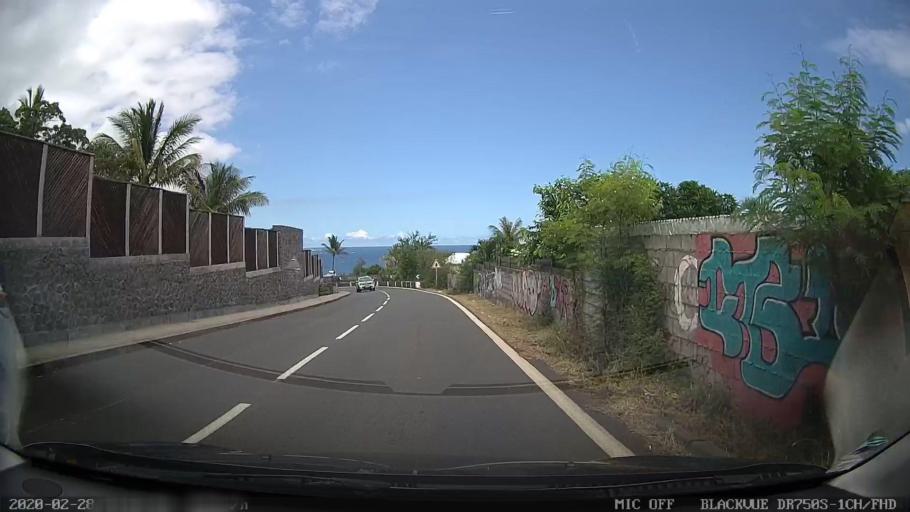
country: RE
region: Reunion
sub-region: Reunion
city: Saint-Leu
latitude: -21.1473
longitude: 55.2768
